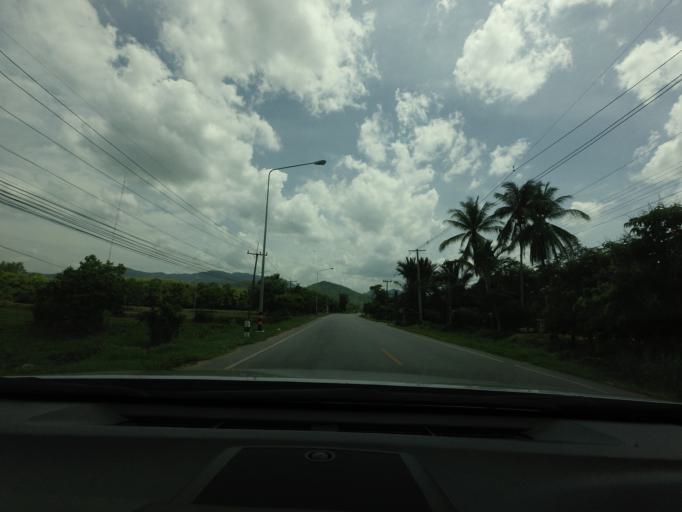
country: TH
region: Yala
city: Raman
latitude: 6.4565
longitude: 101.3597
